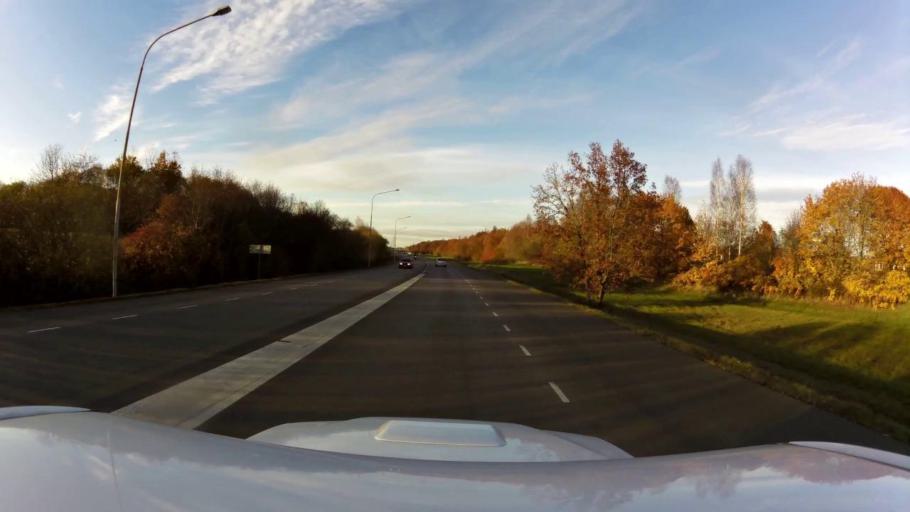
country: SE
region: OEstergoetland
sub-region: Linkopings Kommun
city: Sturefors
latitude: 58.3748
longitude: 15.6892
